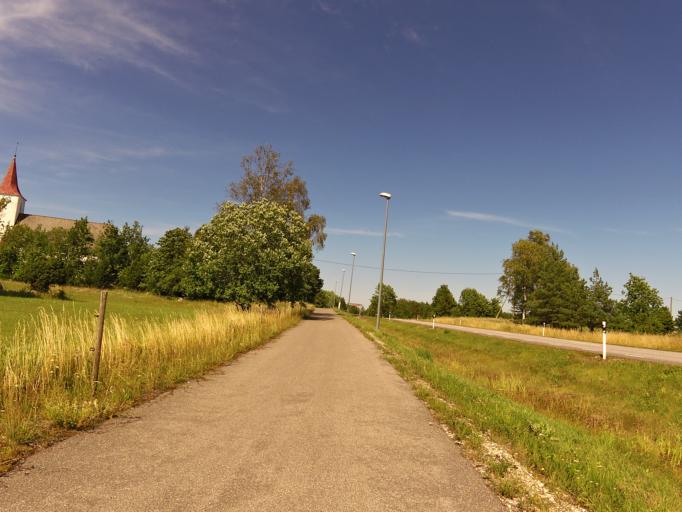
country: EE
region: Hiiumaa
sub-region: Kaerdla linn
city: Kardla
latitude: 58.9816
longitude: 22.5103
